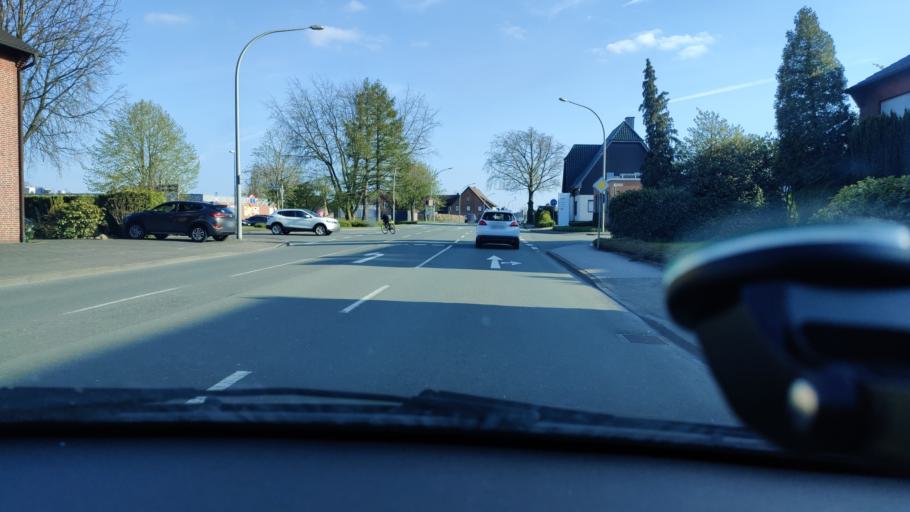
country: DE
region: North Rhine-Westphalia
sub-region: Regierungsbezirk Munster
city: Klein Reken
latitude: 51.8278
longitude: 7.0468
